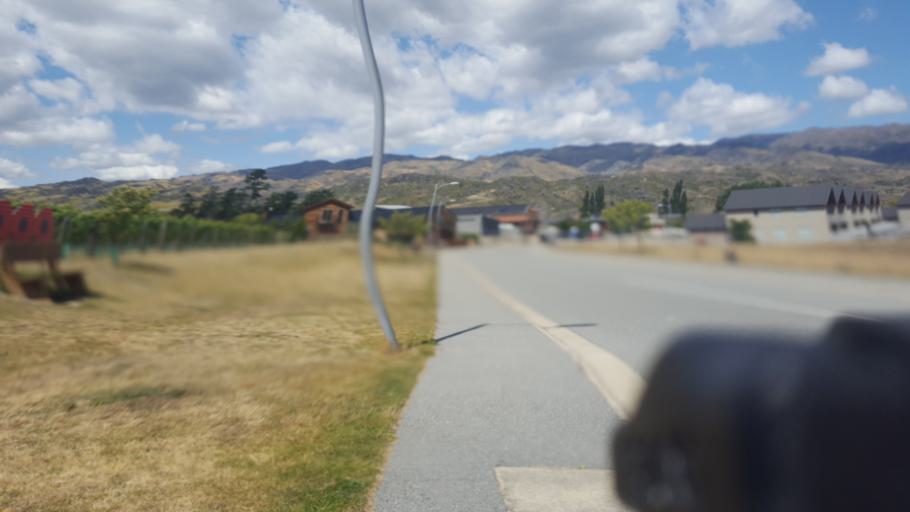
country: NZ
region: Otago
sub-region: Queenstown-Lakes District
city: Wanaka
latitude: -44.9789
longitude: 169.2362
